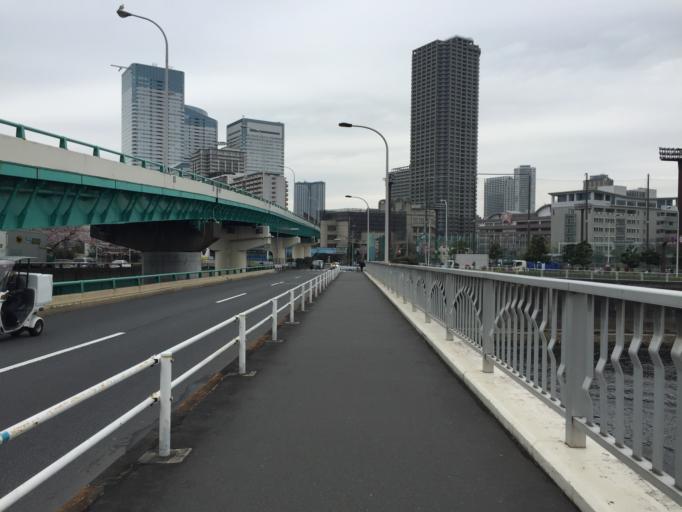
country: JP
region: Tokyo
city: Urayasu
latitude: 35.6590
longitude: 139.7892
